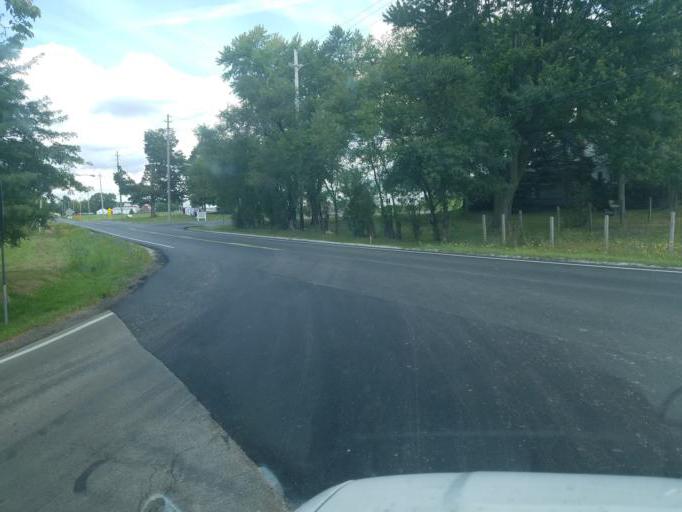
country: US
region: Ohio
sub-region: Geauga County
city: Middlefield
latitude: 41.4253
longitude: -81.1055
